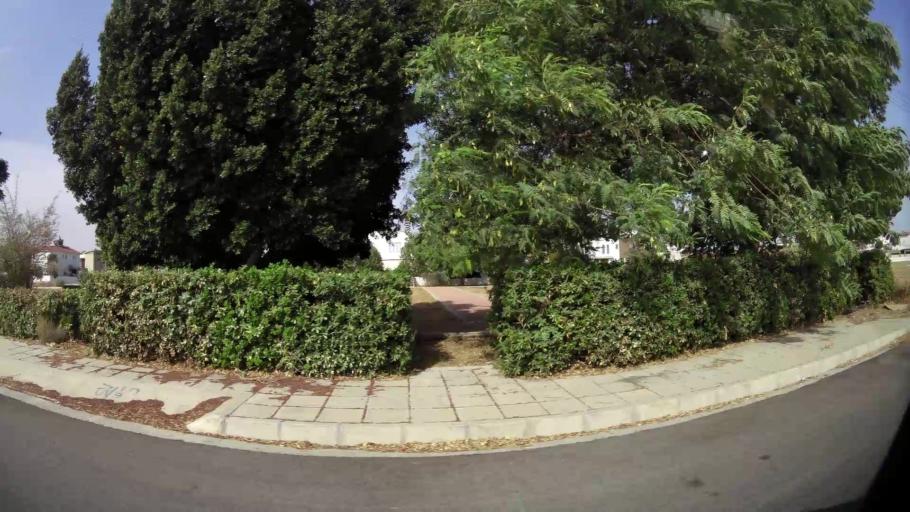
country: CY
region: Lefkosia
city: Geri
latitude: 35.0692
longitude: 33.3979
